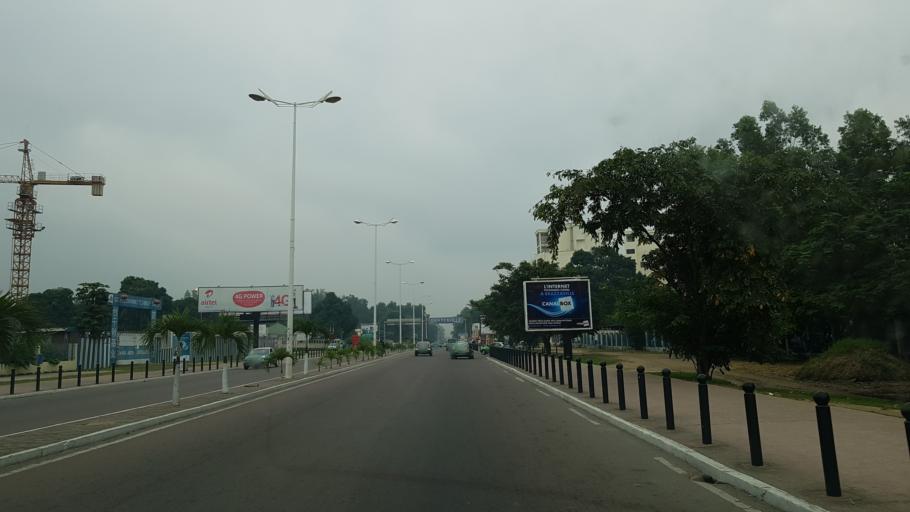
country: CG
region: Brazzaville
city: Brazzaville
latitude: -4.2623
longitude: 15.2523
